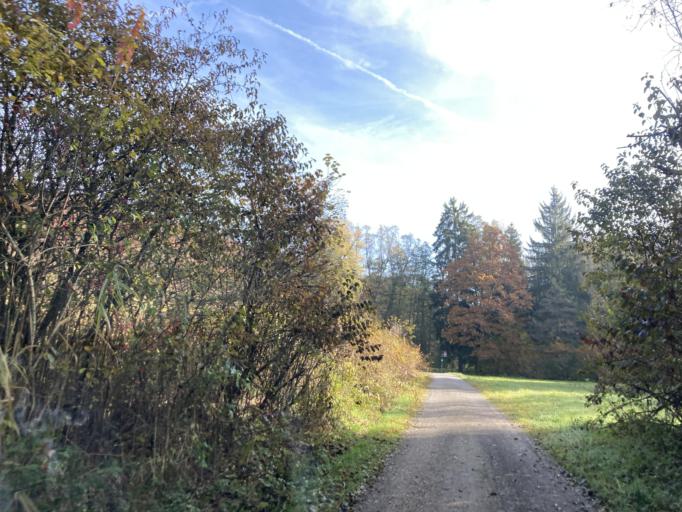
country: DE
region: Baden-Wuerttemberg
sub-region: Tuebingen Region
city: Bodelshausen
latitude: 48.4260
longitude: 8.9714
